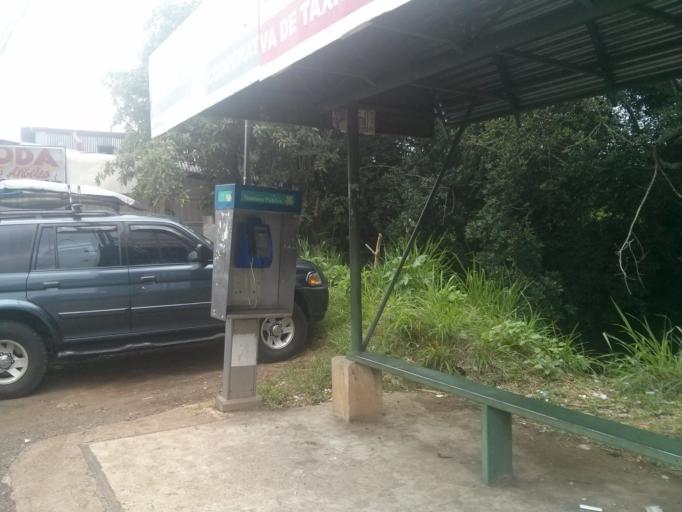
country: CR
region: Alajuela
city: Alajuela
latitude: 10.0190
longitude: -84.1974
